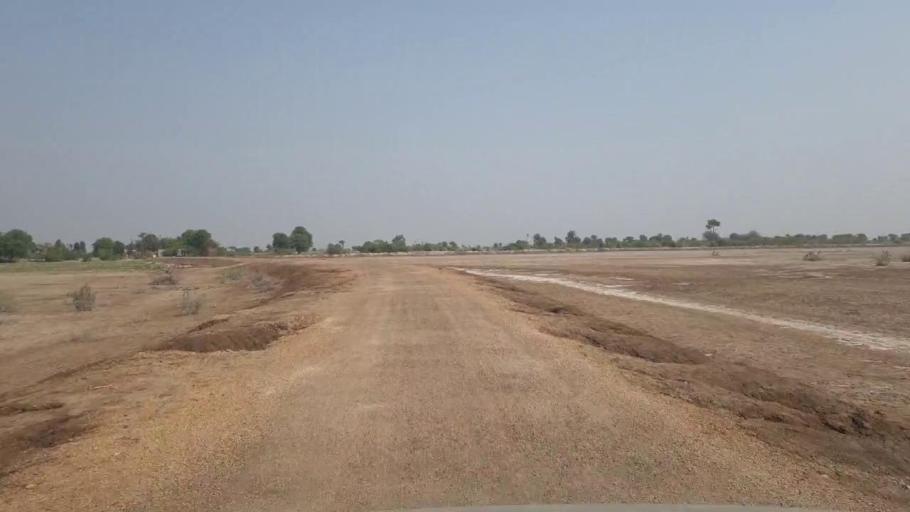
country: PK
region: Sindh
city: Chor
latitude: 25.4833
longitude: 69.7405
